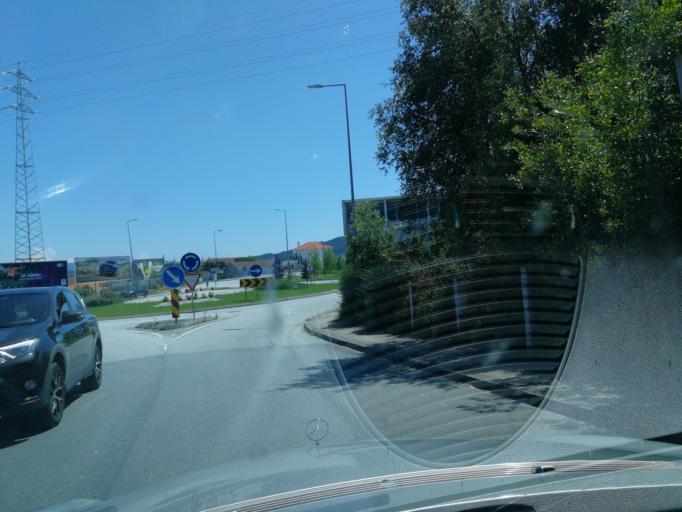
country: PT
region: Viana do Castelo
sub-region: Viana do Castelo
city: Meadela
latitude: 41.7107
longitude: -8.8032
